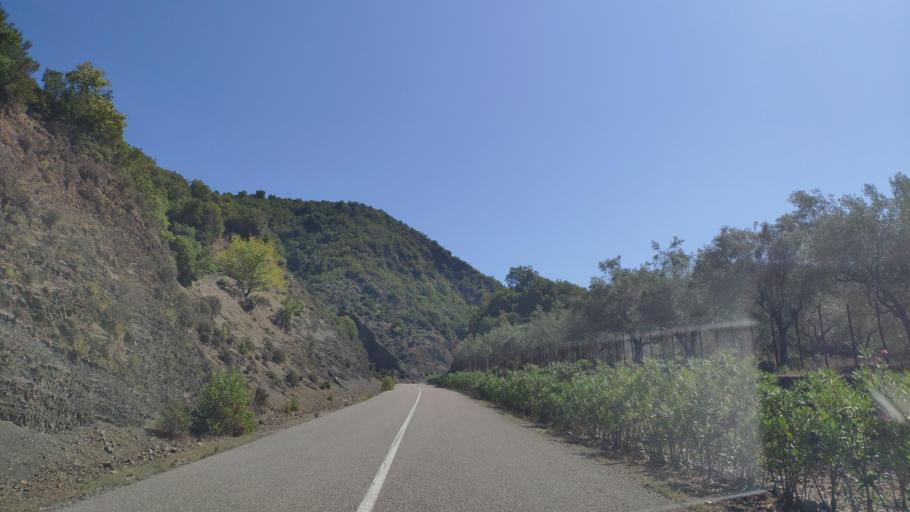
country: GR
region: Central Greece
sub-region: Nomos Evrytanias
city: Kerasochori
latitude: 38.9919
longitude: 21.5050
